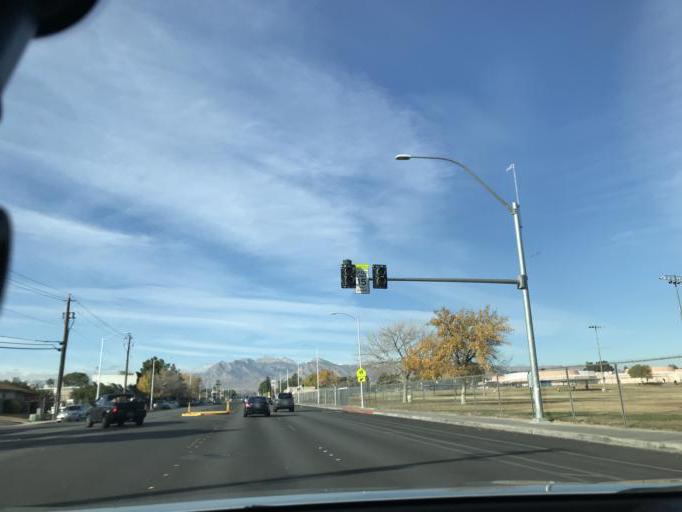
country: US
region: Nevada
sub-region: Clark County
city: Las Vegas
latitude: 36.2031
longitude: -115.2247
